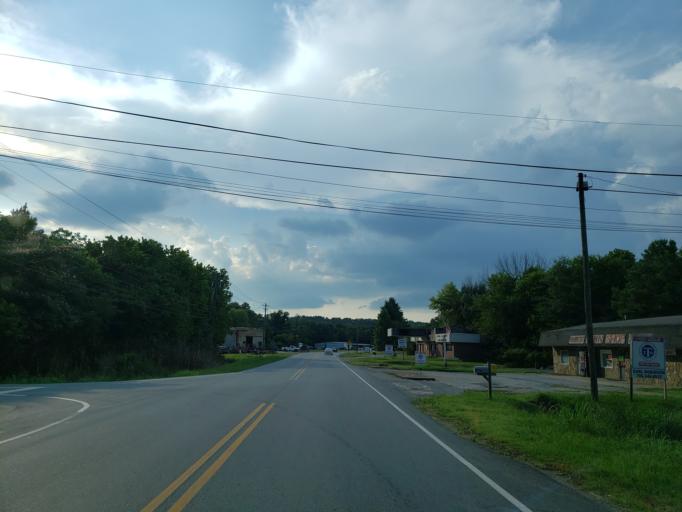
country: US
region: Georgia
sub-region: Polk County
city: Rockmart
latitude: 33.9843
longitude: -85.0397
